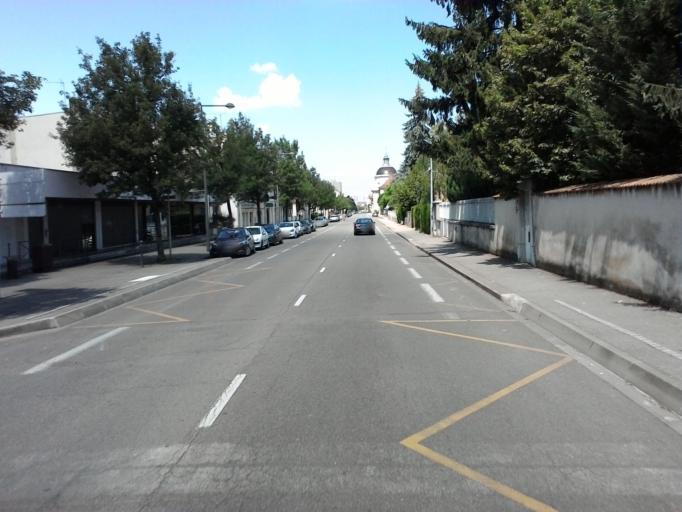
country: FR
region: Rhone-Alpes
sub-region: Departement de l'Ain
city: Bourg-en-Bresse
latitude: 46.1984
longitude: 5.2348
